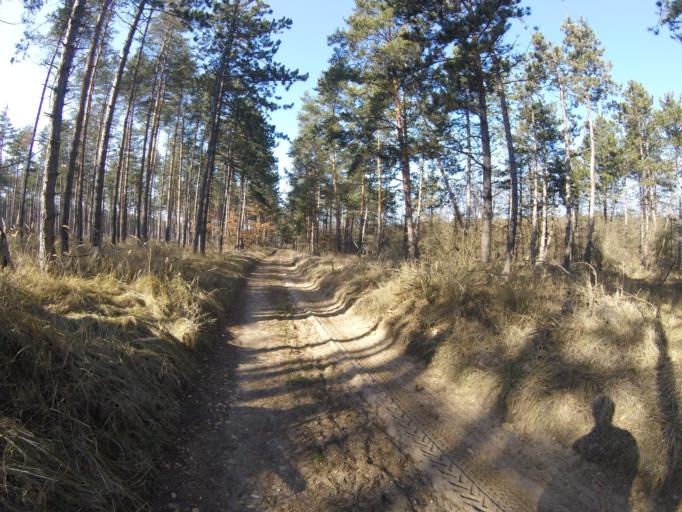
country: HU
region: Komarom-Esztergom
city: Oroszlany
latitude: 47.4577
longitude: 18.3631
